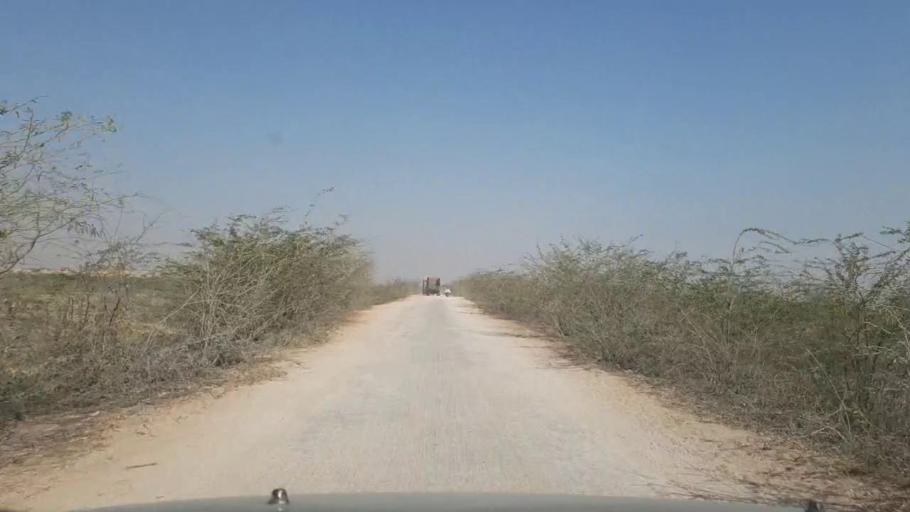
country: PK
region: Sindh
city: Thatta
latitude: 24.9606
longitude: 67.9600
